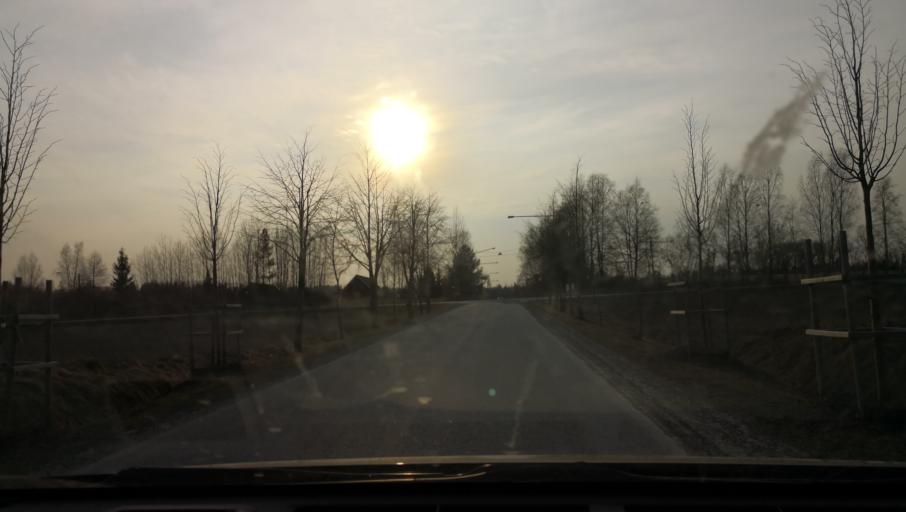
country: SE
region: OErebro
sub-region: Orebro Kommun
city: Hovsta
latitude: 59.3880
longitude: 15.2482
